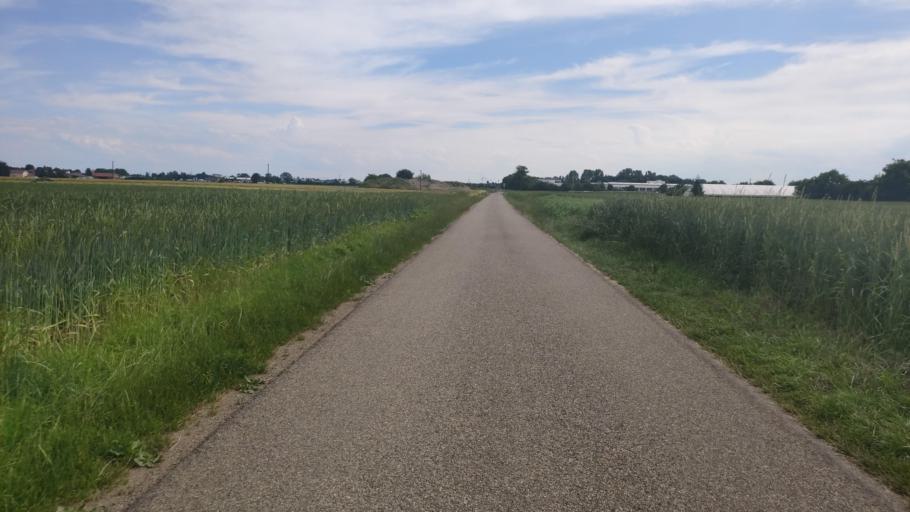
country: DE
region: Bavaria
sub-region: Swabia
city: Konigsbrunn
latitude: 48.2642
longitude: 10.8772
